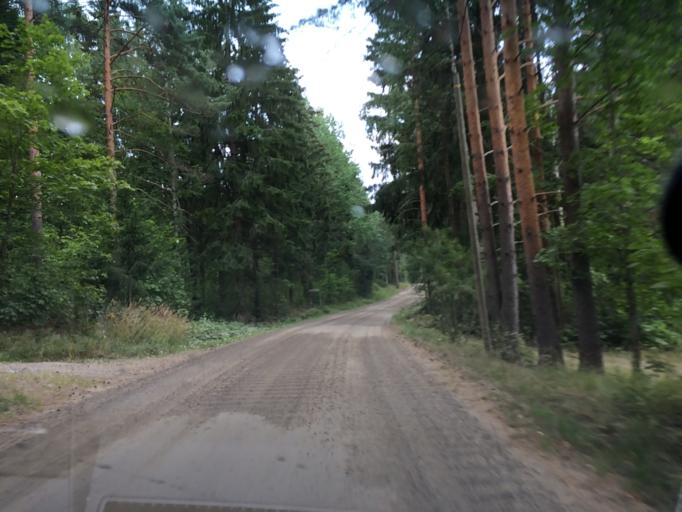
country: FI
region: Pirkanmaa
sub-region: Tampere
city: Luopioinen
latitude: 61.2674
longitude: 24.6868
